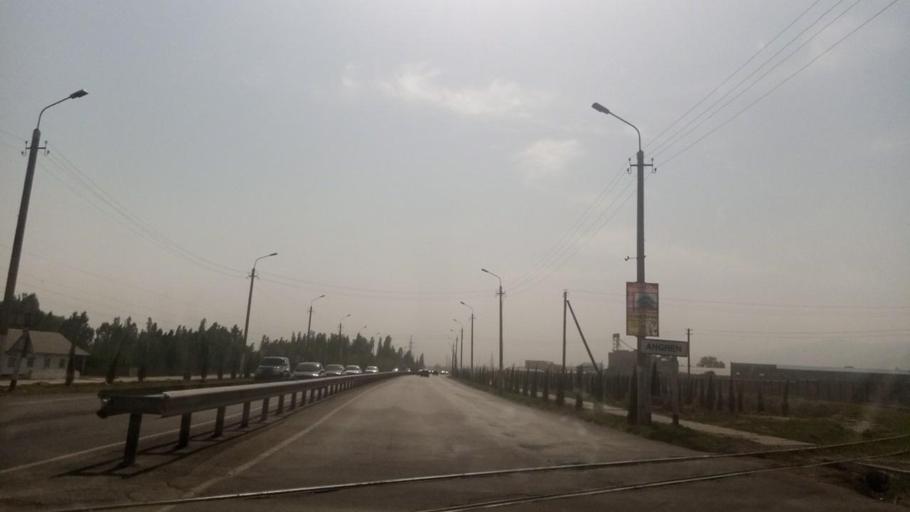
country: UZ
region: Toshkent
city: Angren
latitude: 41.0247
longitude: 70.1322
